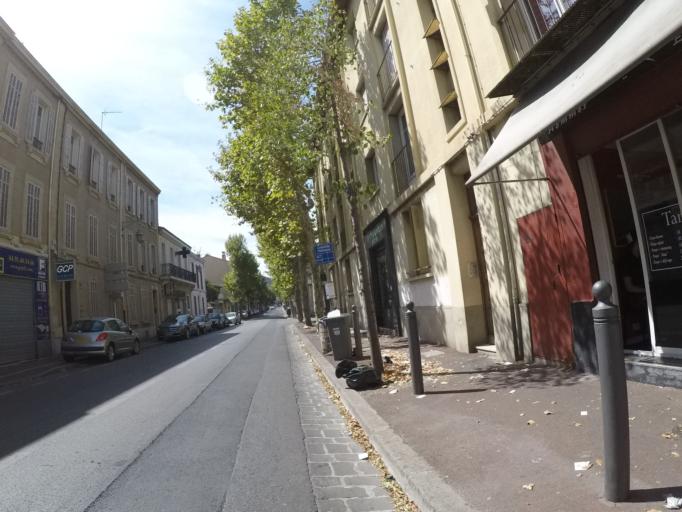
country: FR
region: Provence-Alpes-Cote d'Azur
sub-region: Departement des Bouches-du-Rhone
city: Marseille 09
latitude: 43.2502
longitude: 5.4030
